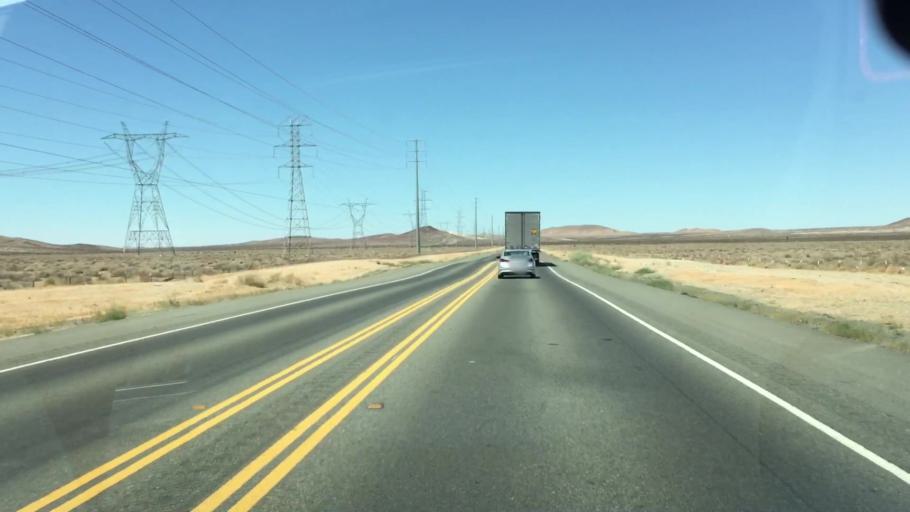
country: US
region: California
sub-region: Kern County
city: Boron
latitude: 34.8273
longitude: -117.4959
